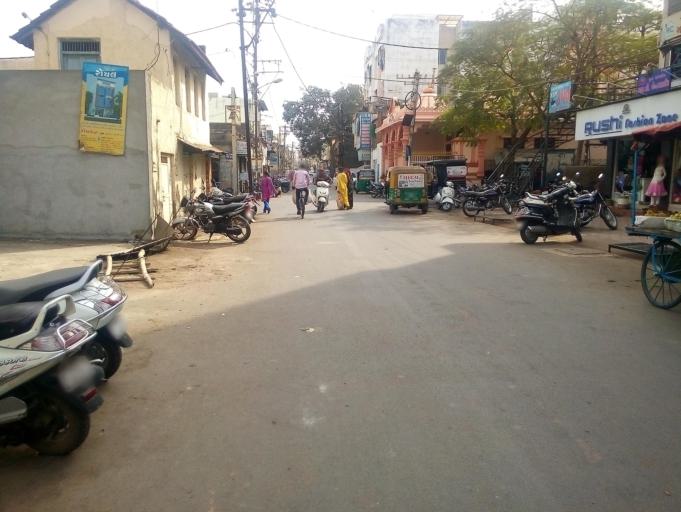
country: IN
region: Gujarat
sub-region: Rajkot
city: Rajkot
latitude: 22.2872
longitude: 70.8081
